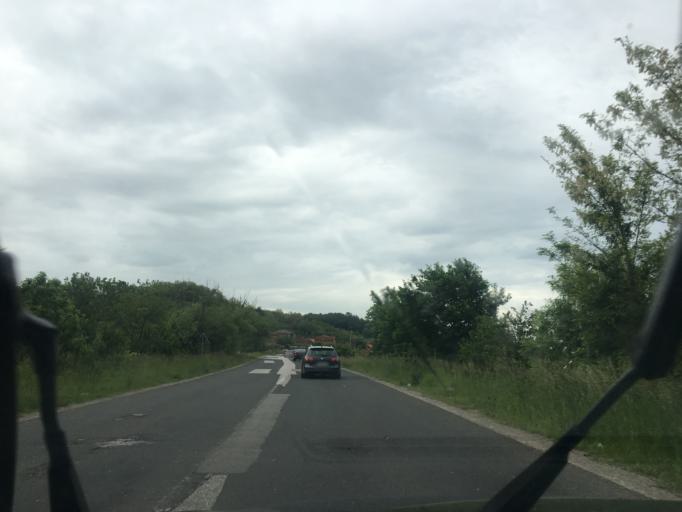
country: XK
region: Pec
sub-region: Komuna e Pejes
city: Kosuriq
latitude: 42.6369
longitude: 20.4415
